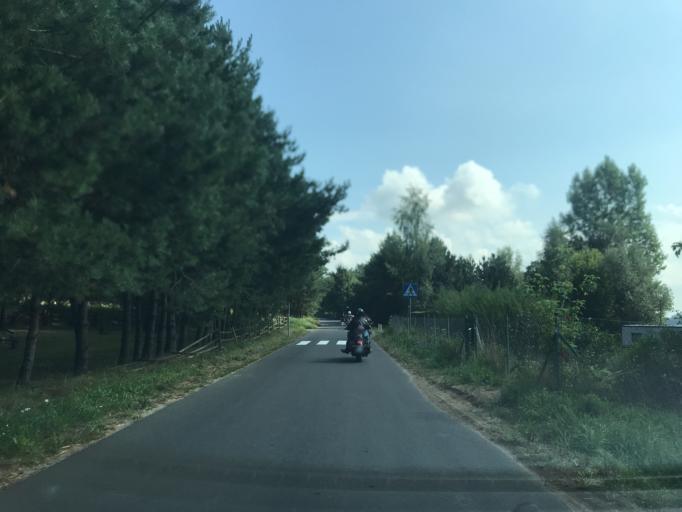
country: PL
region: Warmian-Masurian Voivodeship
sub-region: Powiat nowomiejski
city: Biskupiec
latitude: 53.4518
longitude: 19.4509
